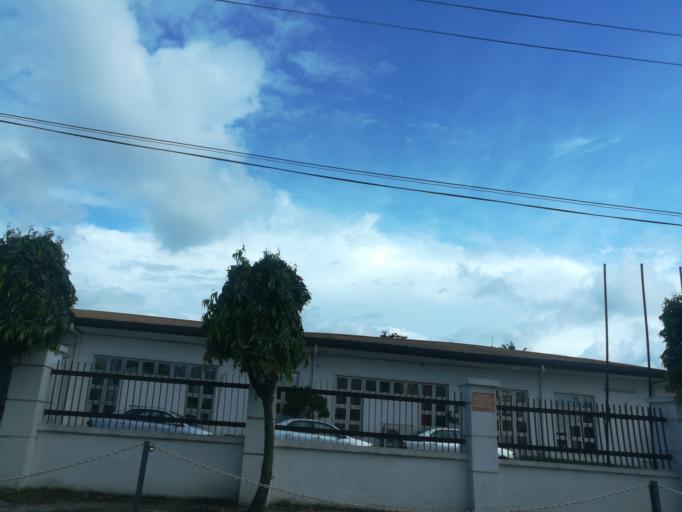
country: NG
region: Lagos
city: Agege
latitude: 6.6246
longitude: 3.3428
